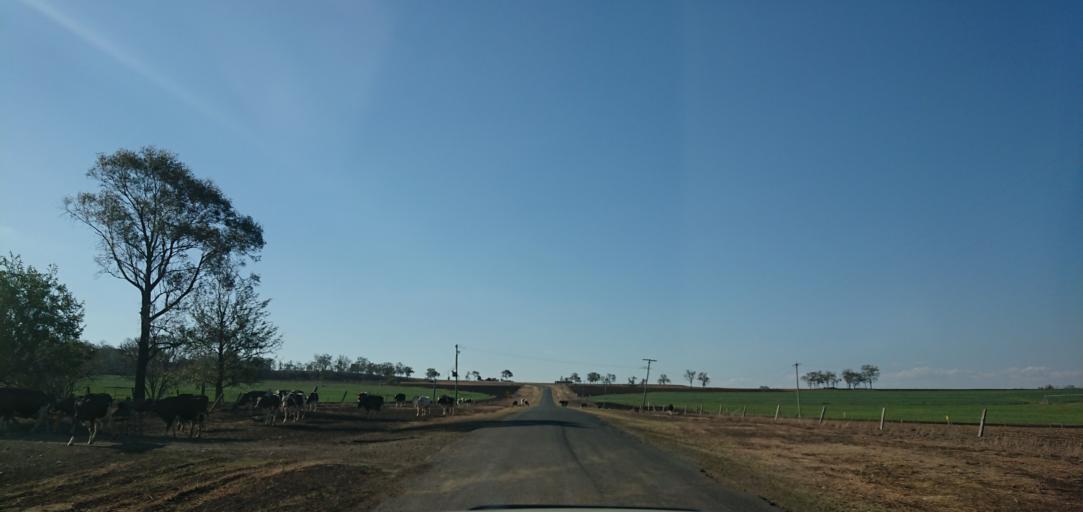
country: AU
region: Queensland
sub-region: Toowoomba
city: Westbrook
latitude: -27.7073
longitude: 151.7163
